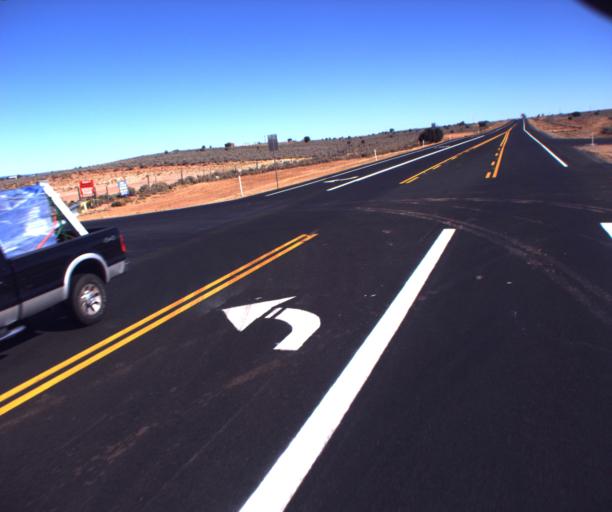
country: US
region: Arizona
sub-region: Apache County
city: Ganado
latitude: 35.7163
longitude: -109.4522
